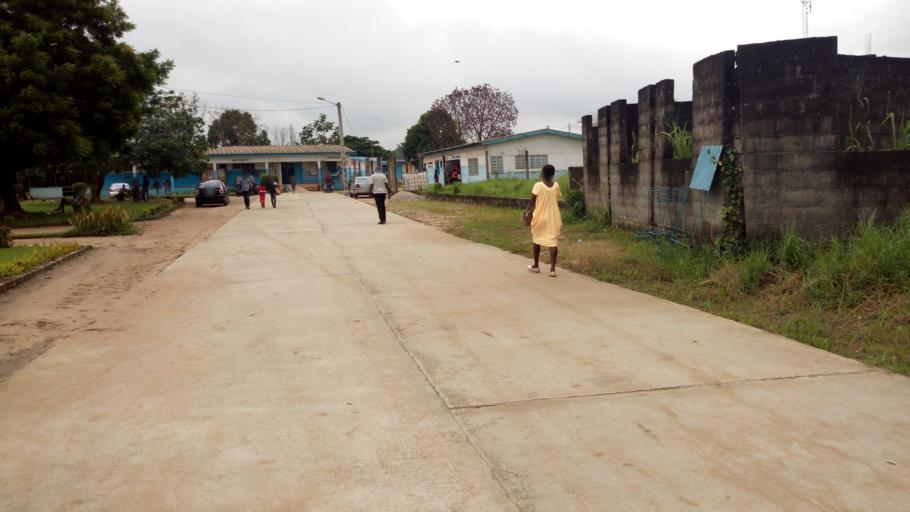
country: CI
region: Lagunes
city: Abobo
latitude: 5.4126
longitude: -3.9954
